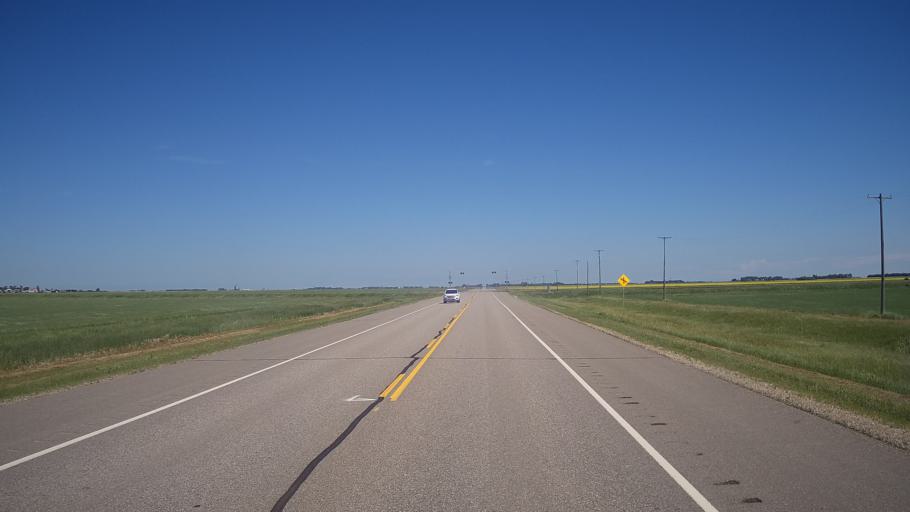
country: CA
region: Manitoba
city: Portage la Prairie
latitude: 50.0070
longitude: -98.4688
